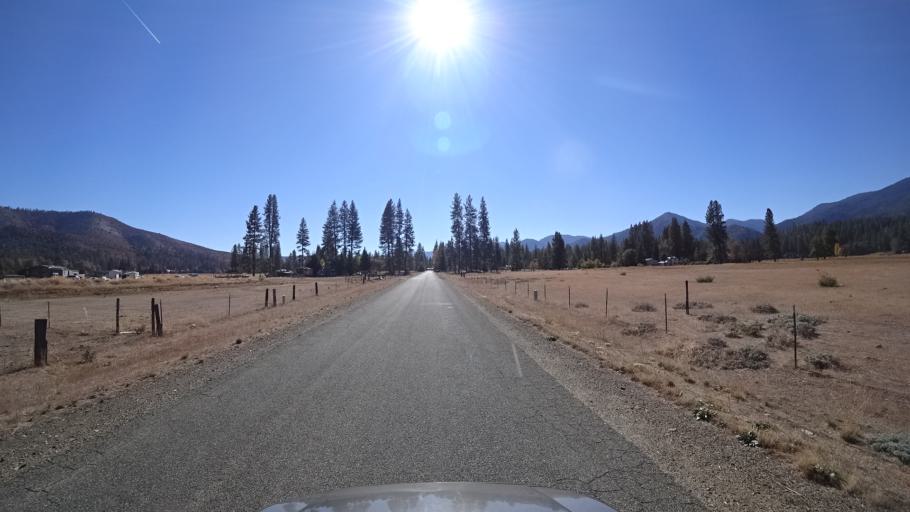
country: US
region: California
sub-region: Siskiyou County
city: Yreka
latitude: 41.6086
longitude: -122.9699
